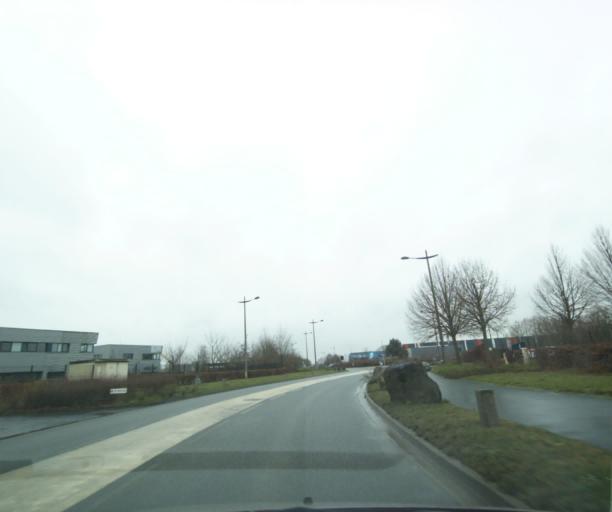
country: FR
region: Nord-Pas-de-Calais
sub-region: Departement du Nord
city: Herin
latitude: 50.3395
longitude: 3.4546
